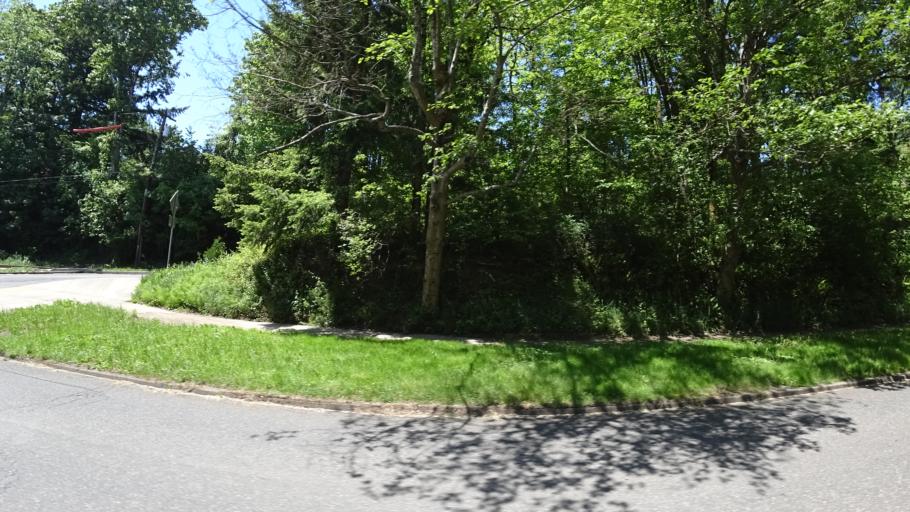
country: US
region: Oregon
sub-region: Multnomah County
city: Portland
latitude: 45.4728
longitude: -122.6854
